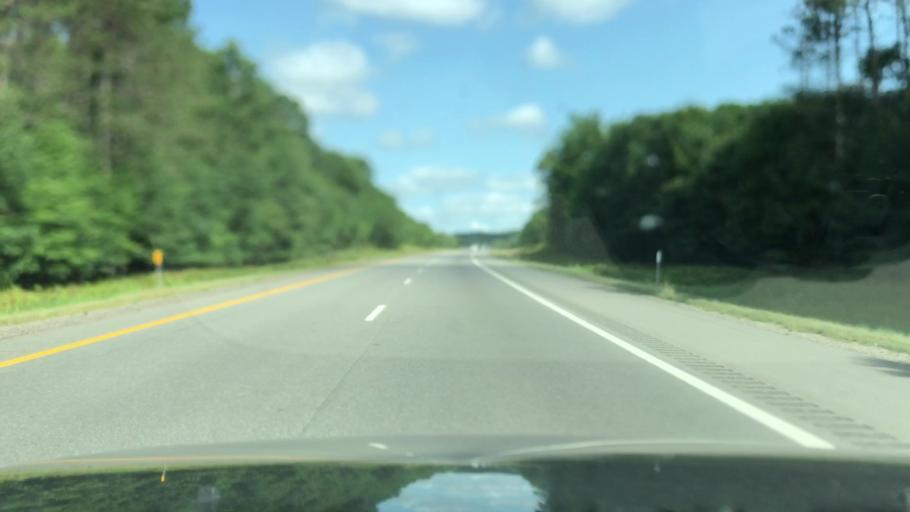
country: US
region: Michigan
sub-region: Mecosta County
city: Big Rapids
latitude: 43.6146
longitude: -85.4960
